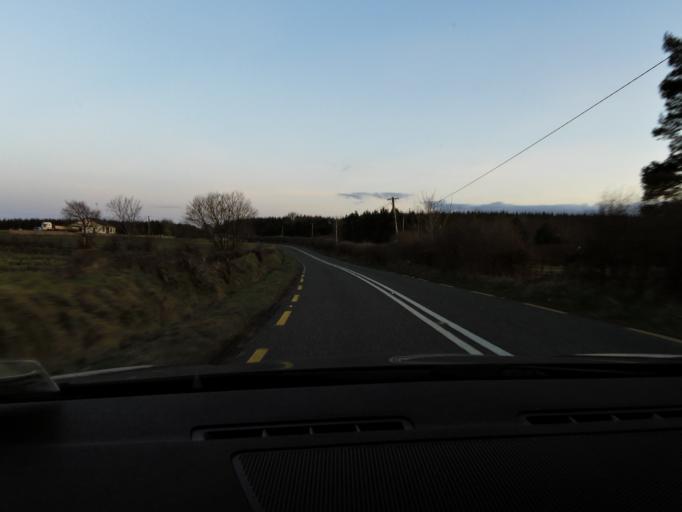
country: IE
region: Connaught
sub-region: Roscommon
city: Boyle
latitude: 53.9130
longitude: -8.2709
